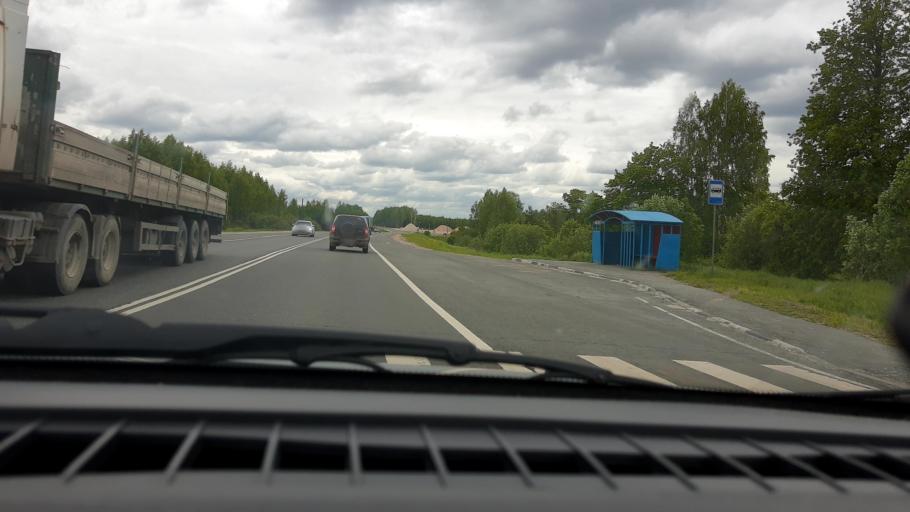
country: RU
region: Nizjnij Novgorod
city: Krasnyye Baki
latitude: 57.0853
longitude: 45.1473
